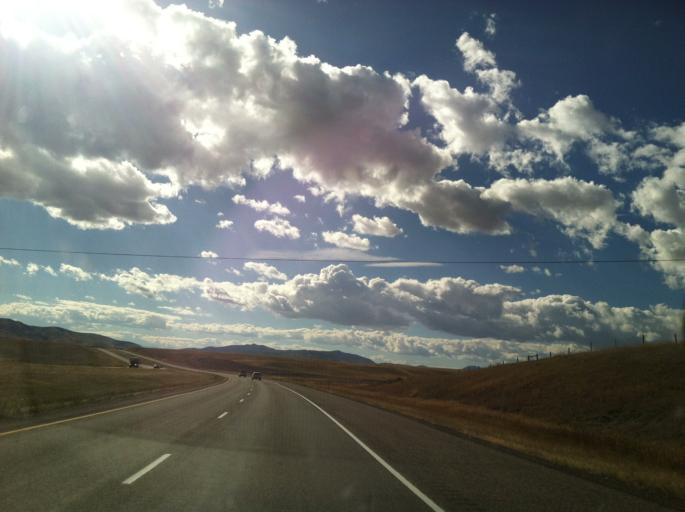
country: US
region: Montana
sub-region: Gallatin County
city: Three Forks
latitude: 45.9201
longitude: -111.7033
